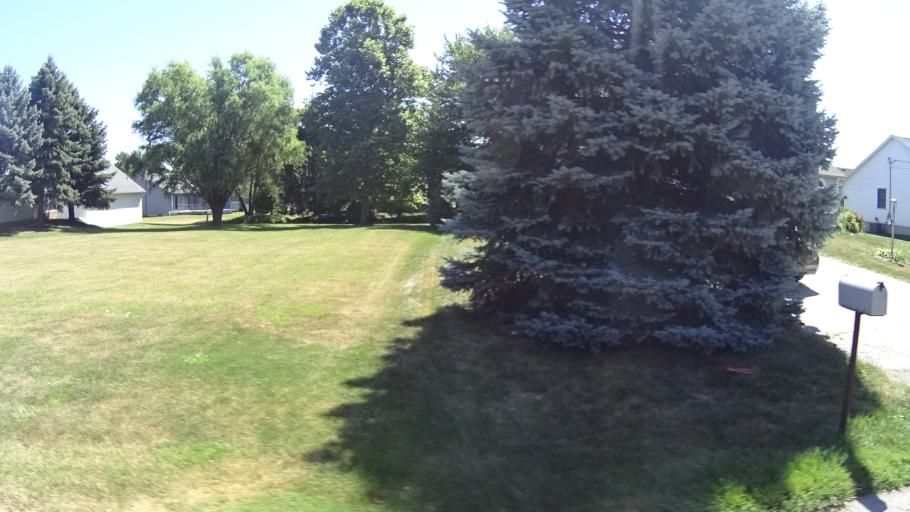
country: US
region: Ohio
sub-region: Erie County
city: Sandusky
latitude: 41.4195
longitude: -82.7032
